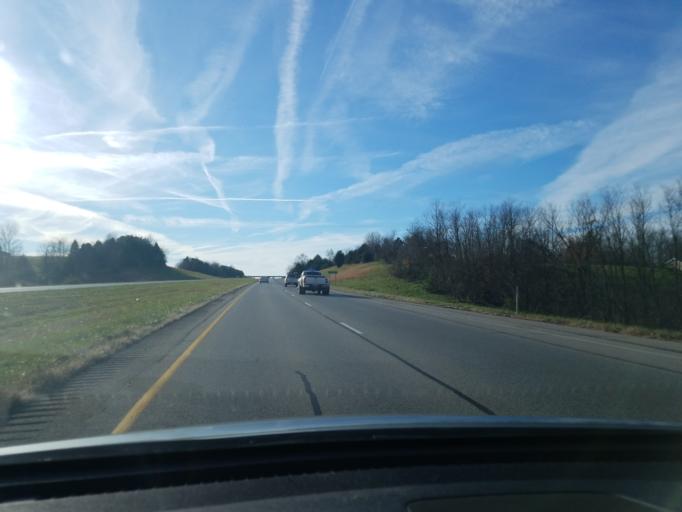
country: US
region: Indiana
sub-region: Floyd County
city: Georgetown
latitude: 38.2717
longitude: -85.9731
